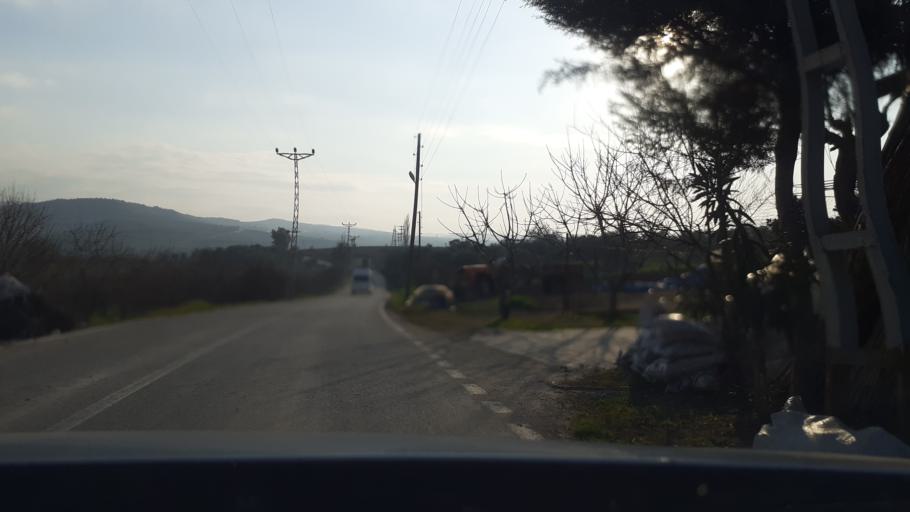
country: TR
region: Hatay
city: Boynuyogun
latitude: 36.1351
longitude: 36.3128
